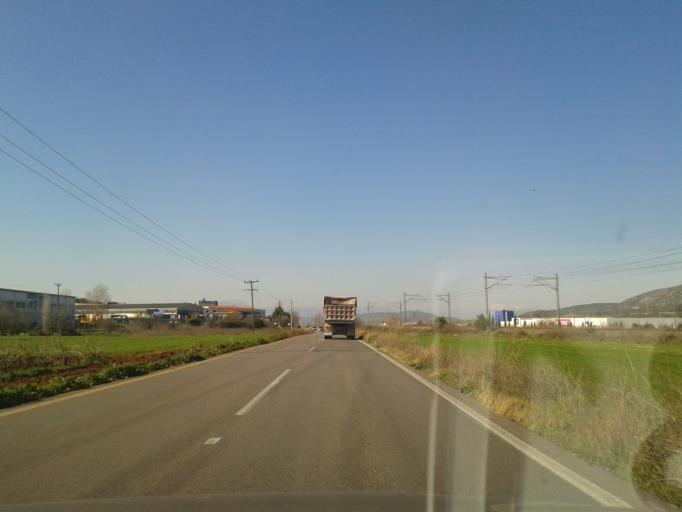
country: GR
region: Central Greece
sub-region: Nomos Voiotias
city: Arma
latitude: 38.3750
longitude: 23.4438
